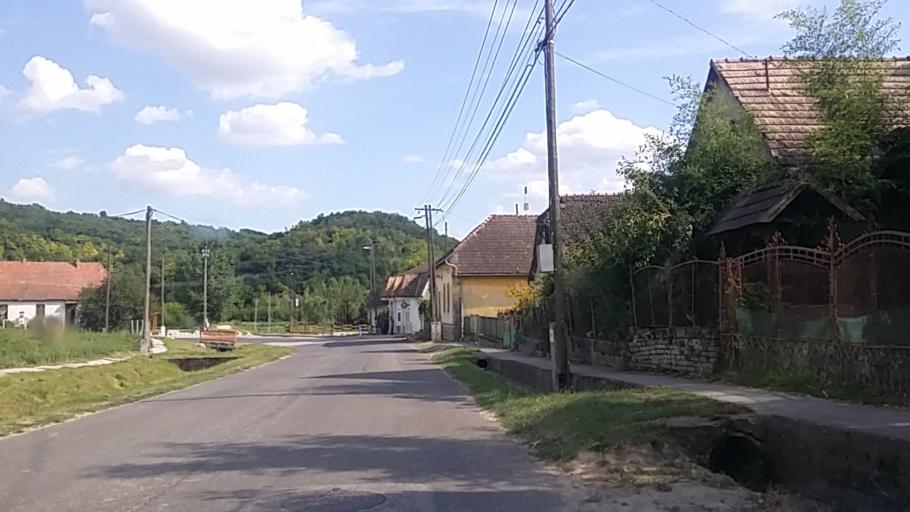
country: HU
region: Tolna
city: Zomba
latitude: 46.5008
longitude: 18.5652
